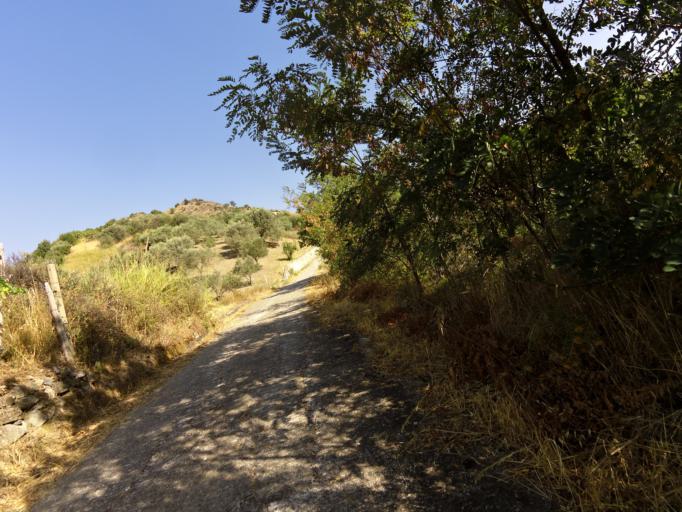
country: IT
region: Calabria
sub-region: Provincia di Reggio Calabria
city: Bivongi
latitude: 38.4931
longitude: 16.4619
